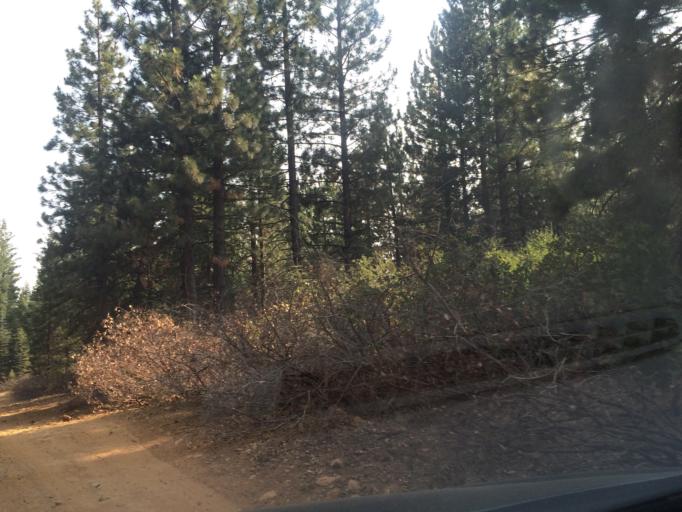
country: US
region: California
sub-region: Sierra County
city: Downieville
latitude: 39.3964
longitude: -120.6607
